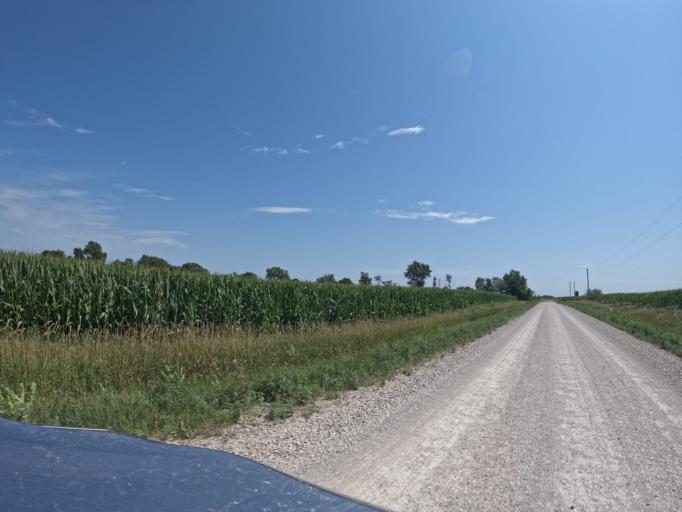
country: US
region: Iowa
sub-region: Henry County
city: Mount Pleasant
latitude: 40.8914
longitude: -91.6318
